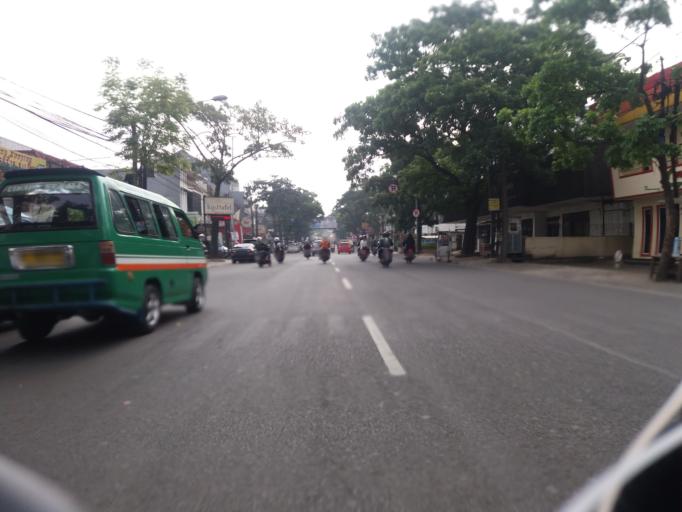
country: ID
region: West Java
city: Bandung
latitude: -6.9101
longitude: 107.5978
